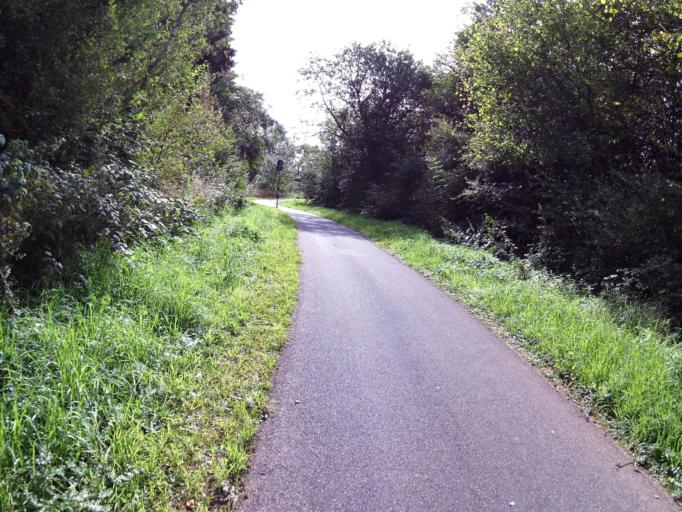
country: DE
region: Rheinland-Pfalz
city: Winterscheid
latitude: 50.2347
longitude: 6.2624
